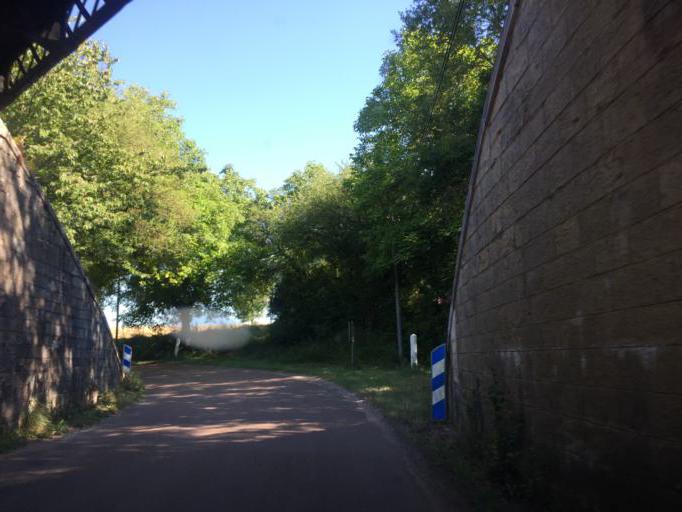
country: FR
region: Bourgogne
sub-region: Departement de l'Yonne
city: Fontenailles
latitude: 47.5022
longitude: 3.3584
